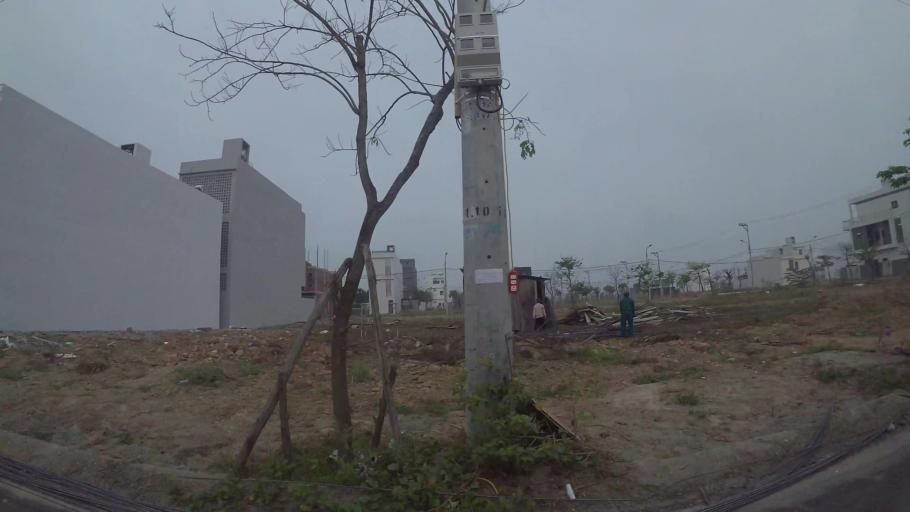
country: VN
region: Da Nang
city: Ngu Hanh Son
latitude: 16.0213
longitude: 108.2352
